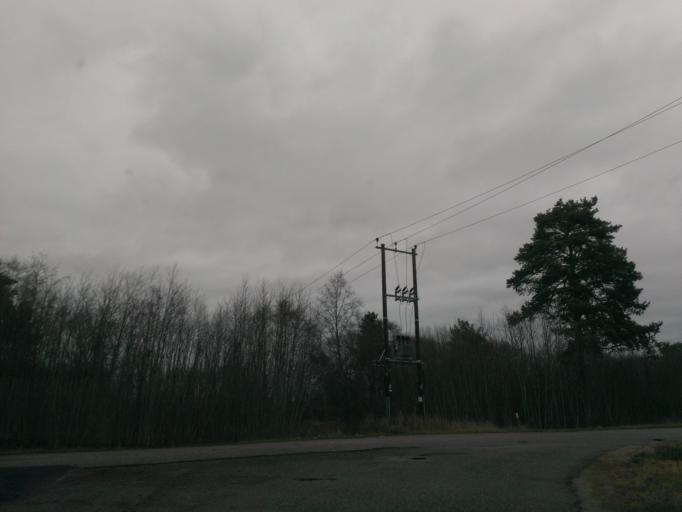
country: LV
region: Adazi
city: Adazi
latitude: 57.0645
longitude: 24.3571
